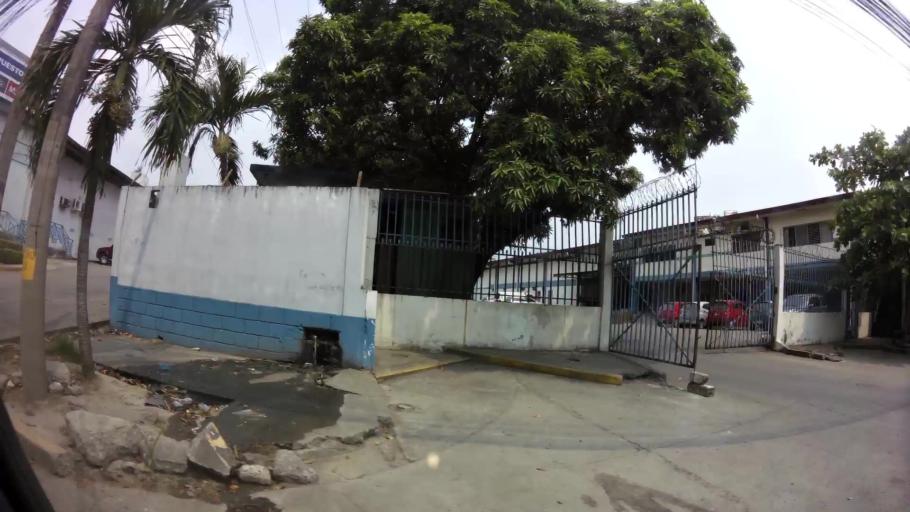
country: HN
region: Cortes
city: San Pedro Sula
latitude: 15.4875
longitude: -88.0280
